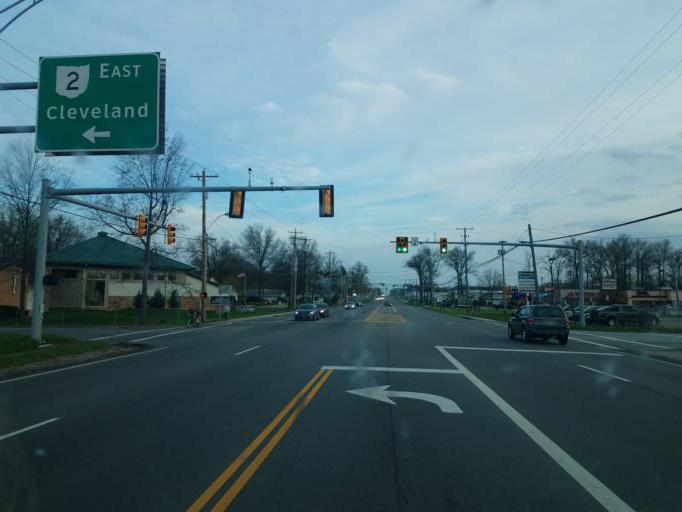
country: US
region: Ohio
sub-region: Lorain County
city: Amherst
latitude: 41.4138
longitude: -82.2091
